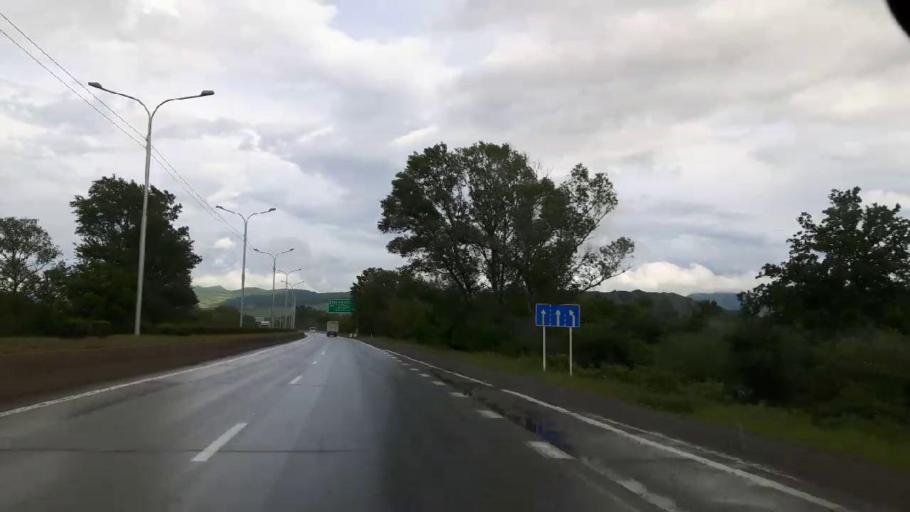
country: GE
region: Shida Kartli
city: Kaspi
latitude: 41.9122
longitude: 44.5634
